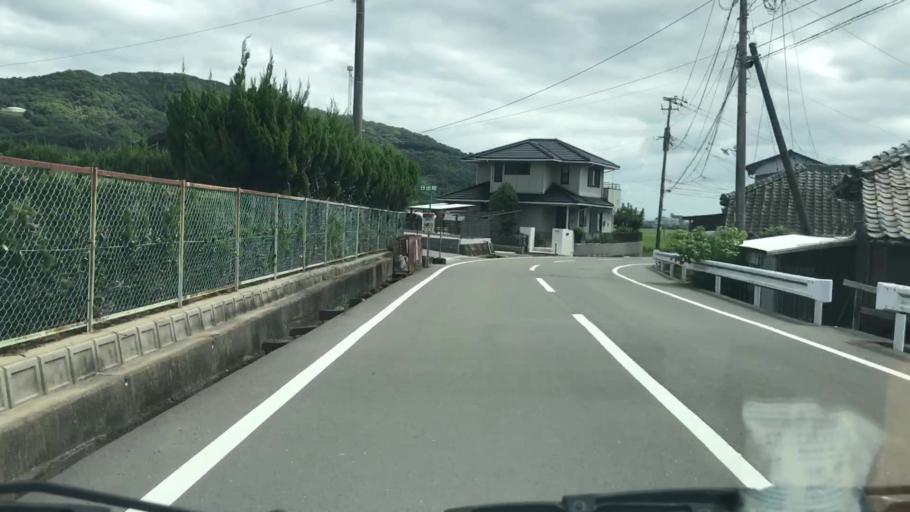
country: JP
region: Saga Prefecture
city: Takeocho-takeo
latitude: 33.2313
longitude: 130.1442
